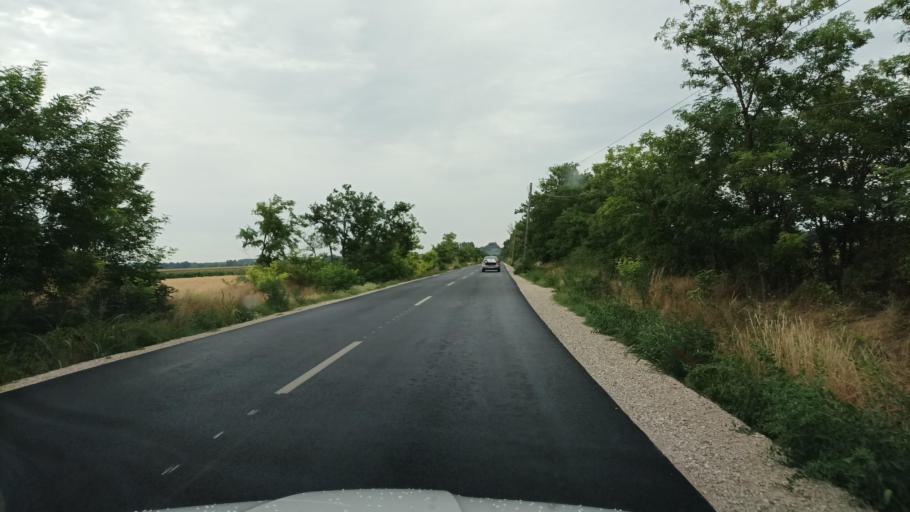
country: HU
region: Pest
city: Dabas
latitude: 47.1960
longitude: 19.2557
